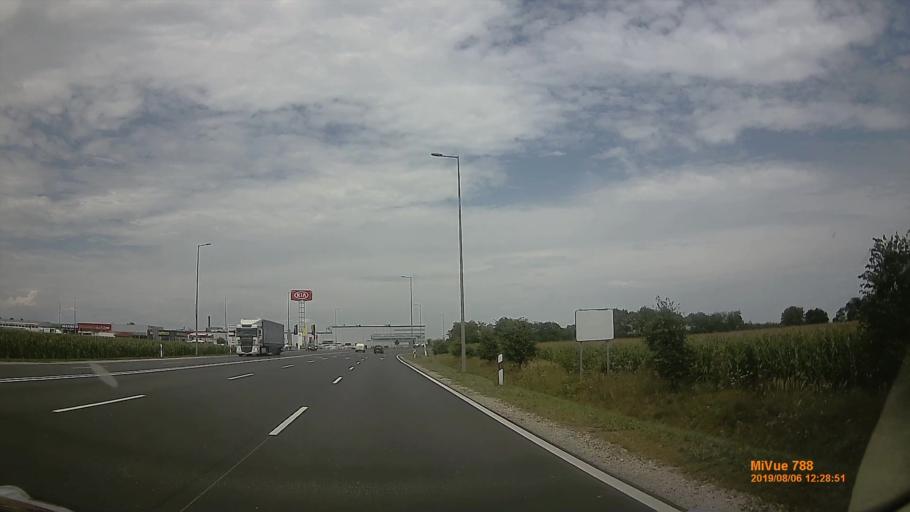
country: HU
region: Vas
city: Szombathely
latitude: 47.2266
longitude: 16.6567
